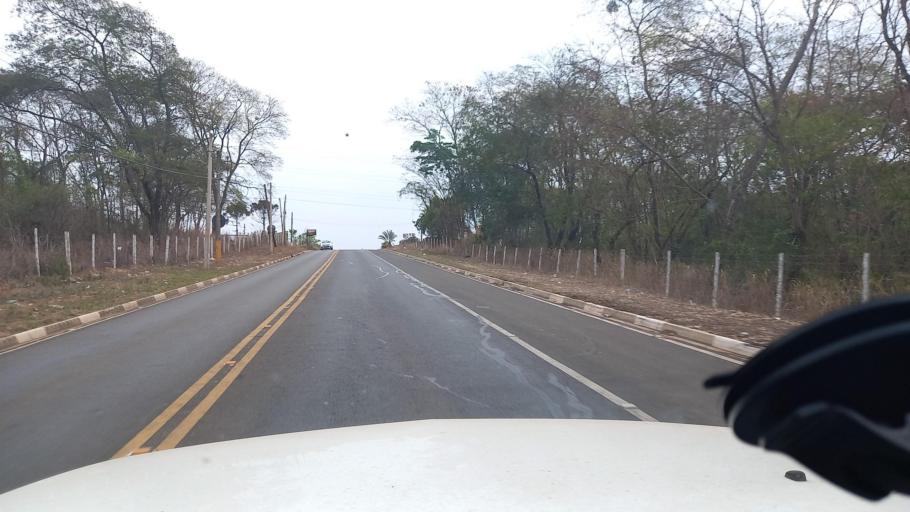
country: BR
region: Sao Paulo
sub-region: Moji-Guacu
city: Mogi-Gaucu
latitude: -22.3741
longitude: -46.9676
